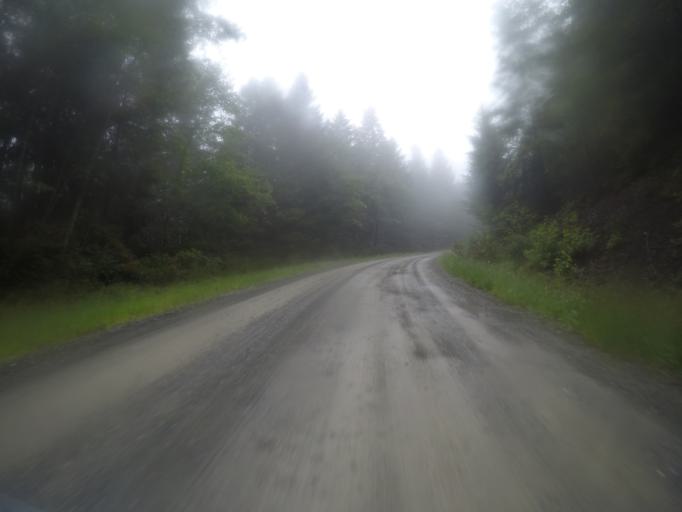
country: US
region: California
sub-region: Humboldt County
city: Westhaven-Moonstone
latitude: 41.2424
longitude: -123.9889
